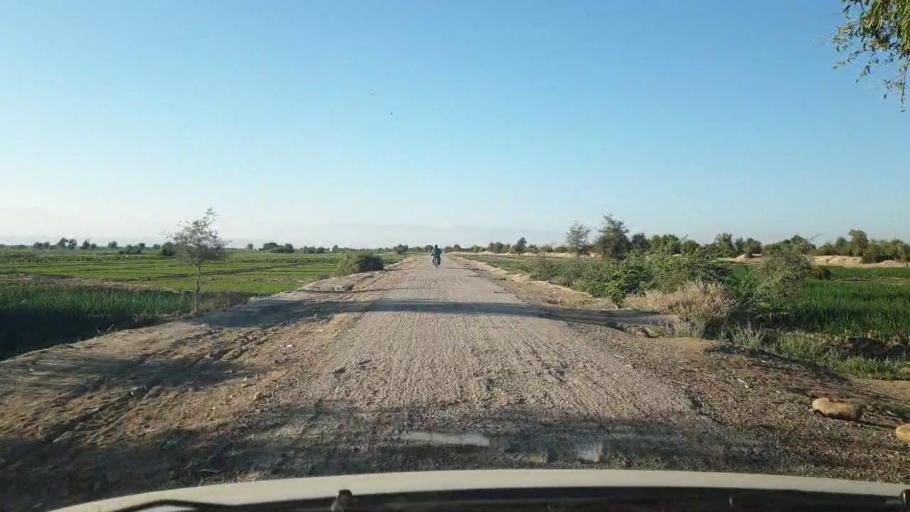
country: PK
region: Sindh
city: Johi
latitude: 26.7624
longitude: 67.4667
